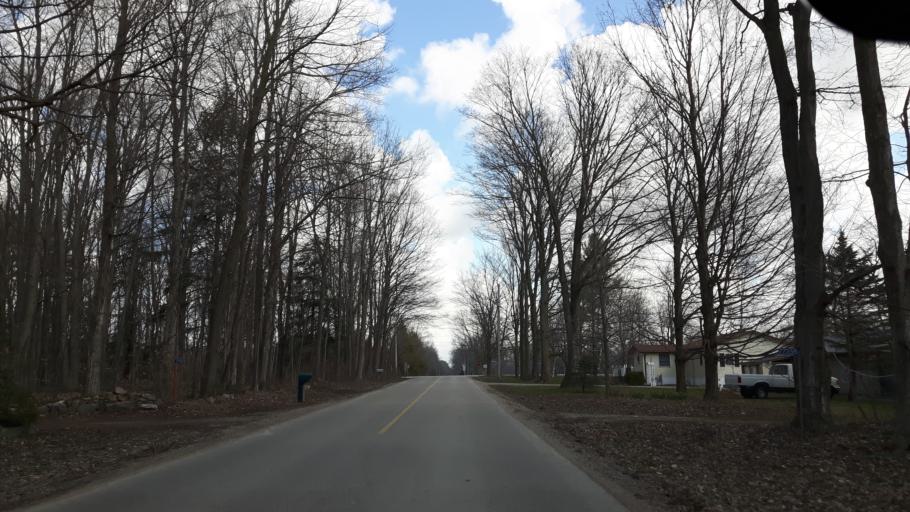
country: CA
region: Ontario
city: Bluewater
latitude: 43.5859
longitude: -81.6848
